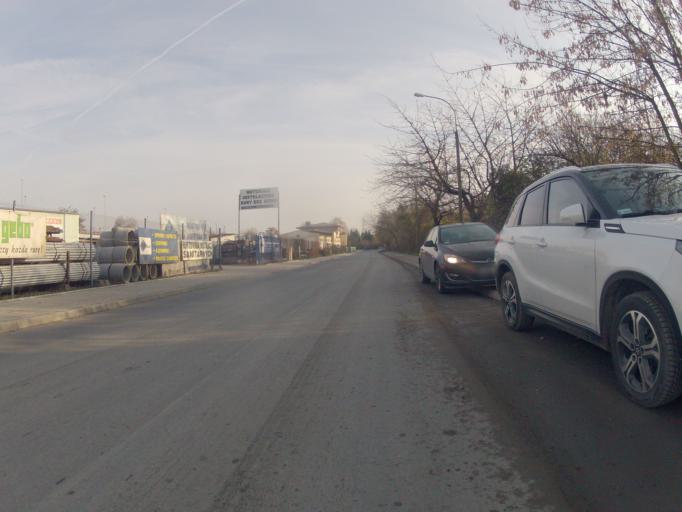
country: PL
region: Lesser Poland Voivodeship
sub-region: Krakow
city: Krakow
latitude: 50.0516
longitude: 19.9776
